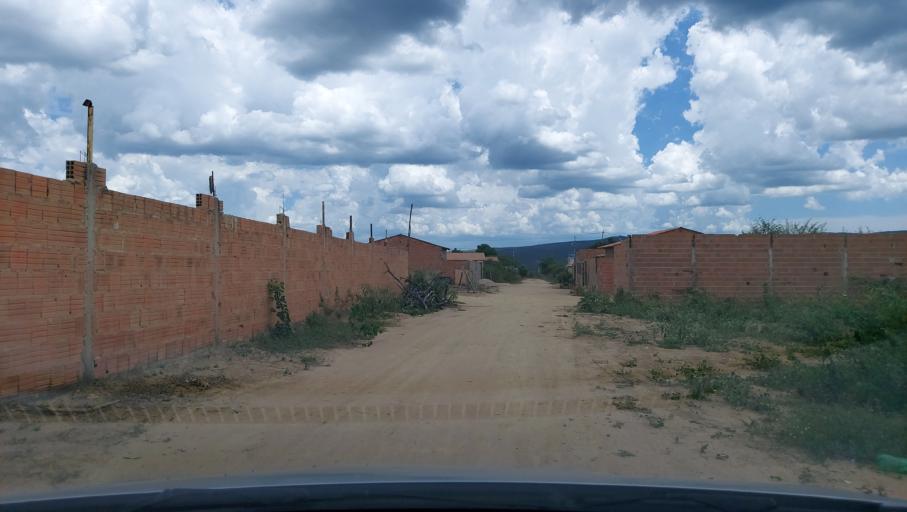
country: BR
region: Bahia
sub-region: Oliveira Dos Brejinhos
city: Beira Rio
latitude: -12.0069
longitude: -42.6339
